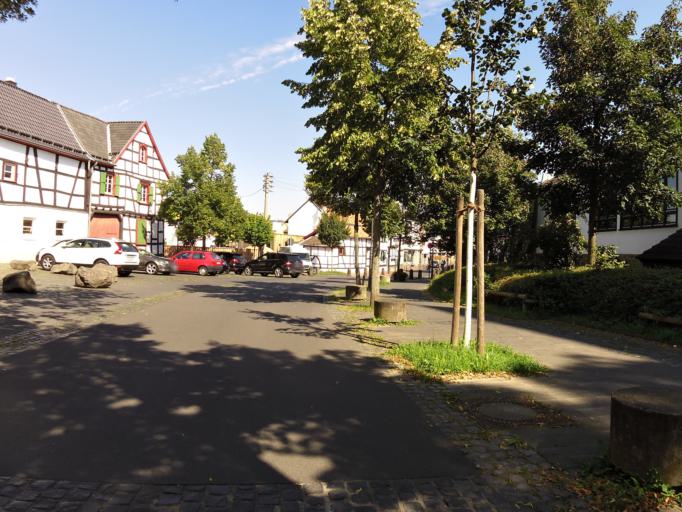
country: DE
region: North Rhine-Westphalia
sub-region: Regierungsbezirk Koln
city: Rheinbach
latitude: 50.6240
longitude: 6.9502
